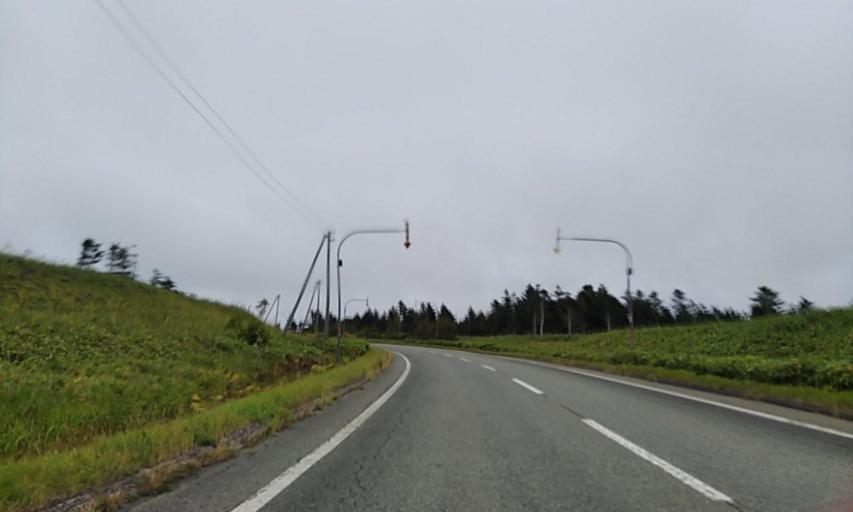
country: JP
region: Hokkaido
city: Makubetsu
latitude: 45.4590
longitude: 141.9951
